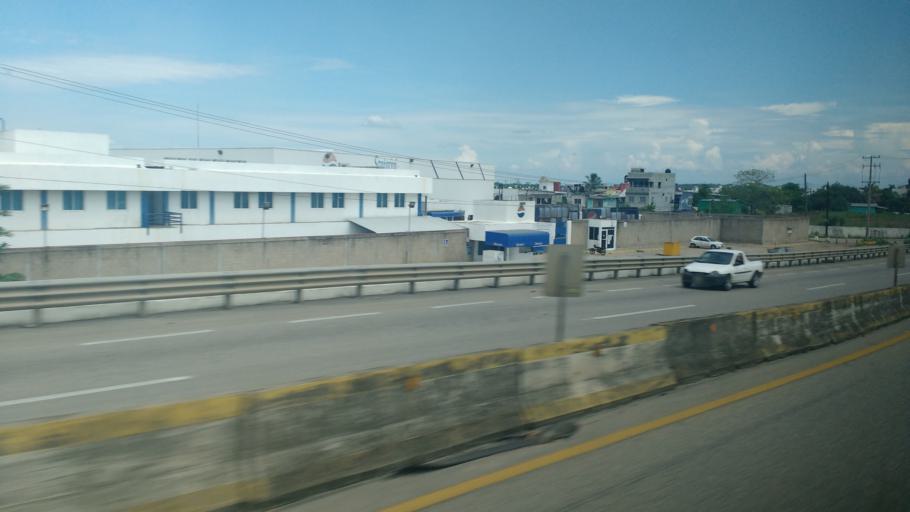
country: MX
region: Tabasco
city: Parrilla
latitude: 17.9066
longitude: -92.9229
